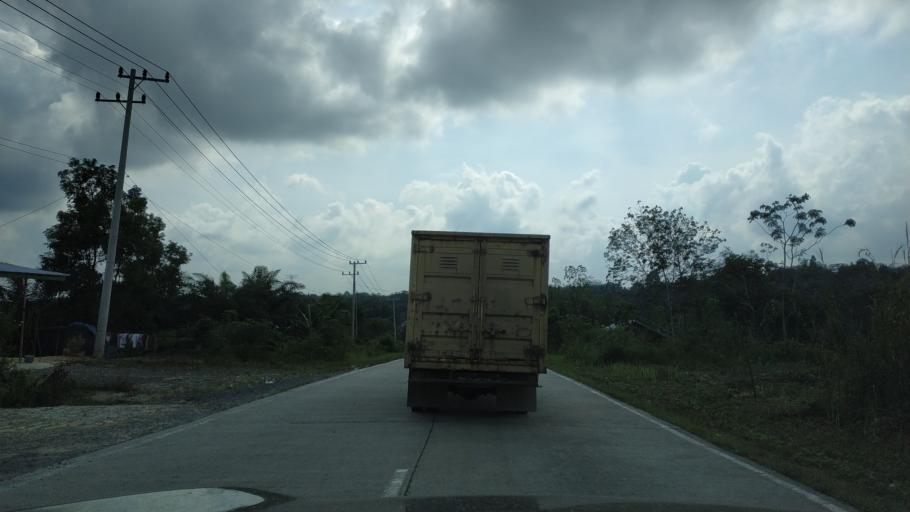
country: ID
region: Riau
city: Pangkalan Kasai
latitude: -0.6964
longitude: 102.4849
